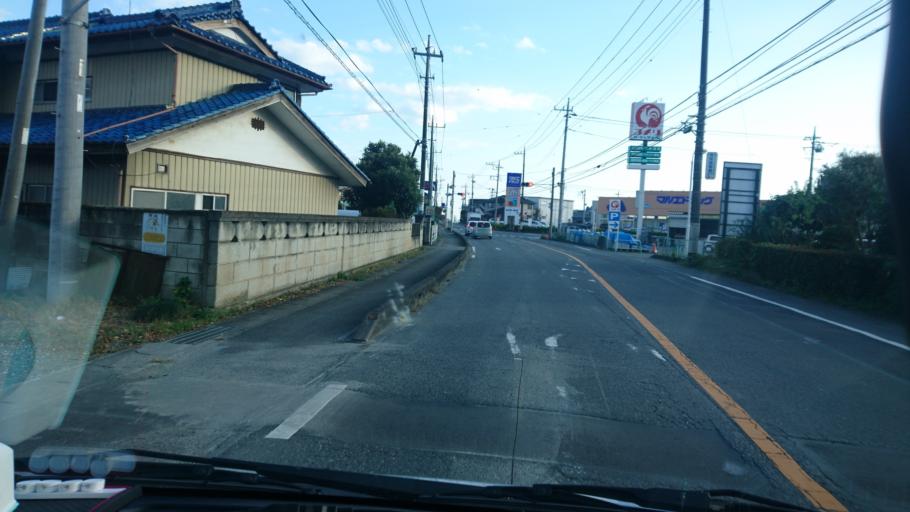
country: JP
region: Gunma
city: Omamacho-omama
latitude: 36.4465
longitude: 139.2753
